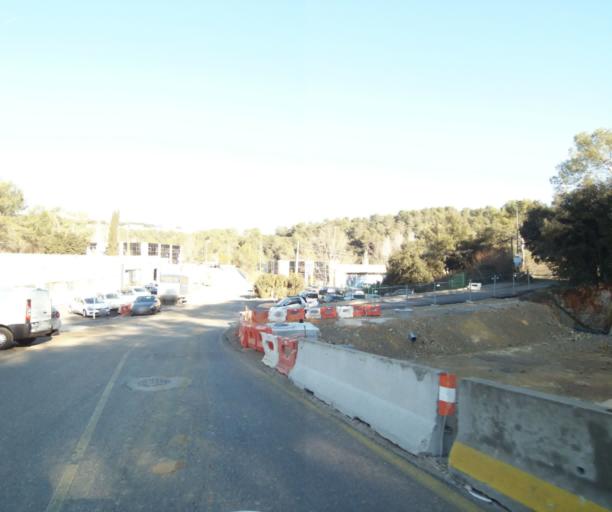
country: FR
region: Provence-Alpes-Cote d'Azur
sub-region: Departement des Alpes-Maritimes
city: Biot
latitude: 43.6095
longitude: 7.0747
